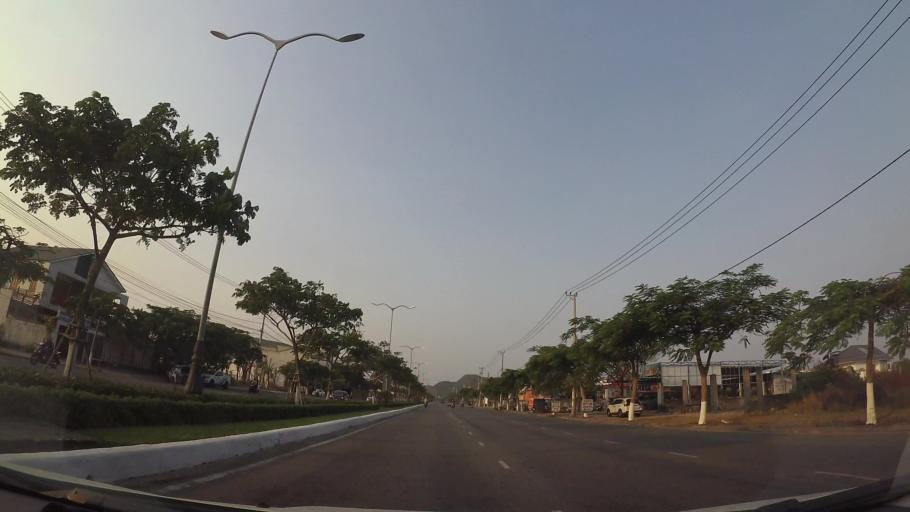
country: VN
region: Da Nang
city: Ngu Hanh Son
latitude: 15.9920
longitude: 108.2581
